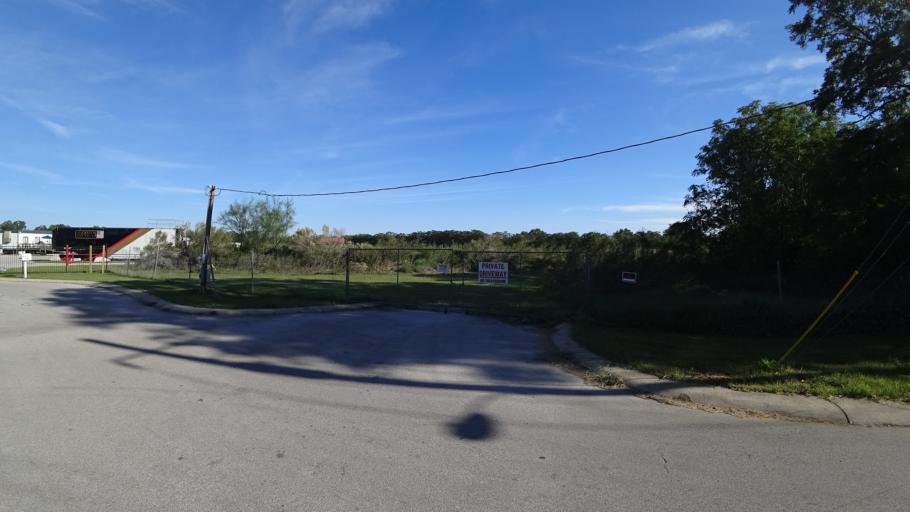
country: US
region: Texas
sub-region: Travis County
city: Hornsby Bend
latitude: 30.2646
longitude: -97.6582
